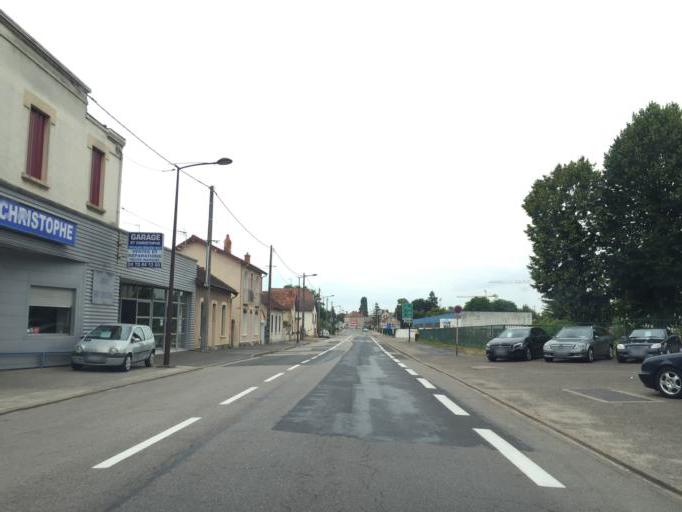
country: FR
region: Auvergne
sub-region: Departement de l'Allier
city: Moulins
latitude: 46.5763
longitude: 3.3246
